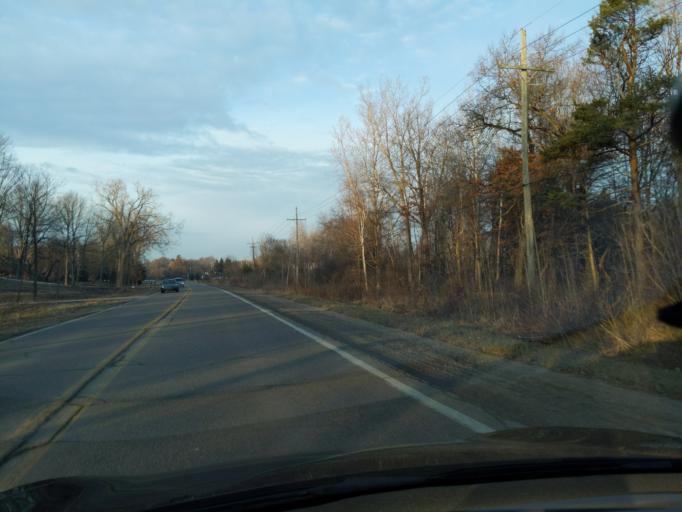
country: US
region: Michigan
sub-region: Livingston County
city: Brighton
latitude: 42.5677
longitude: -83.7530
